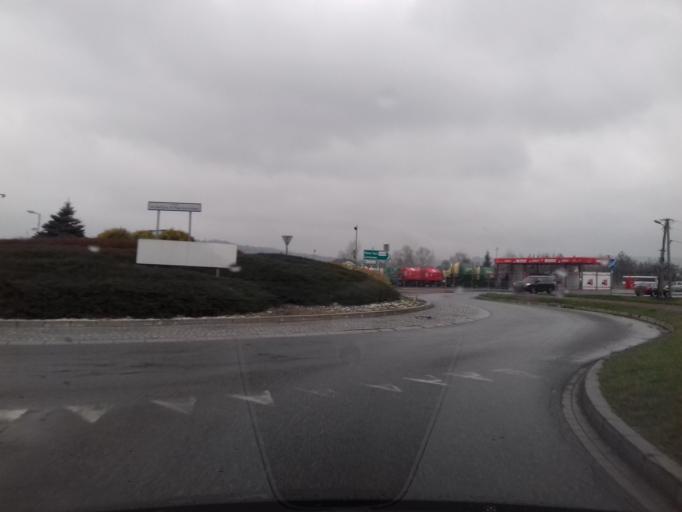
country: PL
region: Lesser Poland Voivodeship
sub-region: Powiat nowosadecki
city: Stary Sacz
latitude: 49.5916
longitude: 20.6295
